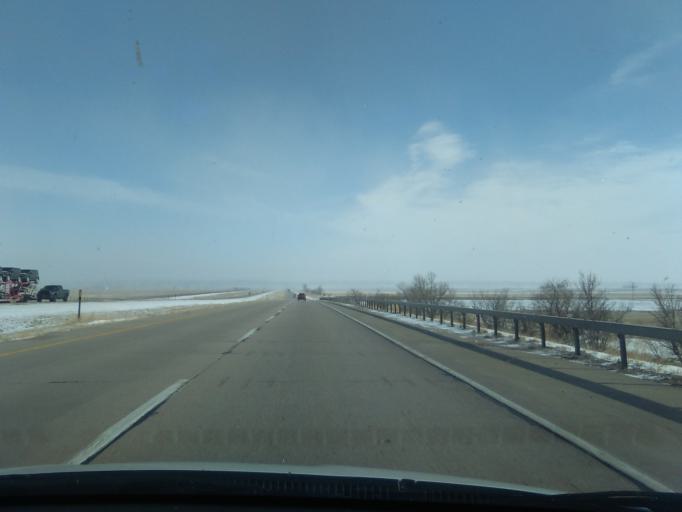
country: US
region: Wyoming
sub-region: Laramie County
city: Pine Bluffs
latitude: 41.1475
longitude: -104.1575
